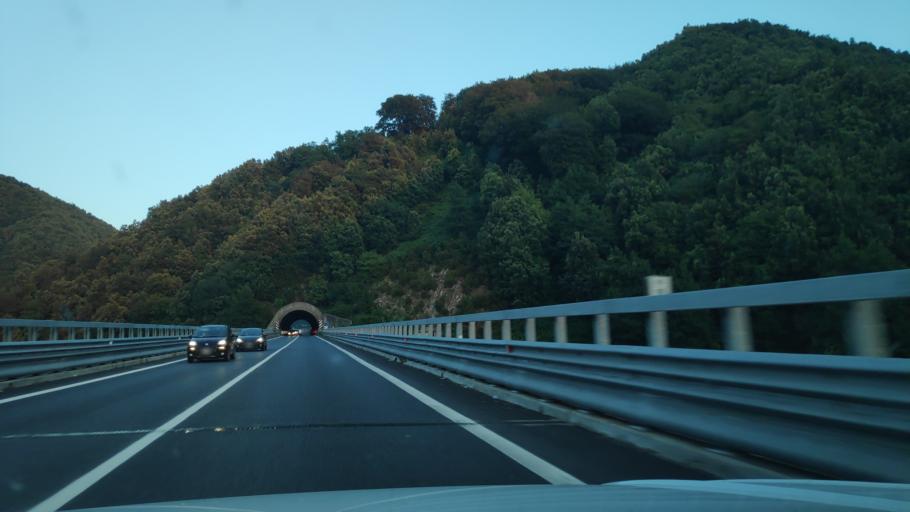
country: IT
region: Calabria
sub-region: Provincia di Reggio Calabria
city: Amato
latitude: 38.4104
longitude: 16.1430
